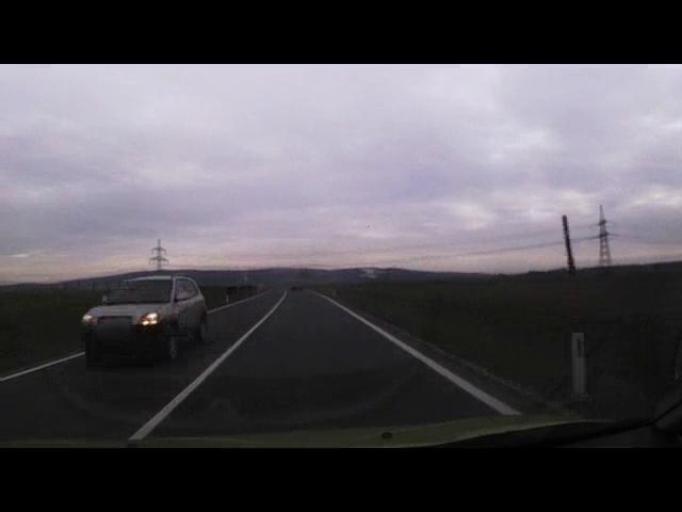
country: AT
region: Burgenland
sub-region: Eisenstadt-Umgebung
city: Neufeld an der Leitha
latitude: 47.8640
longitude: 16.4057
